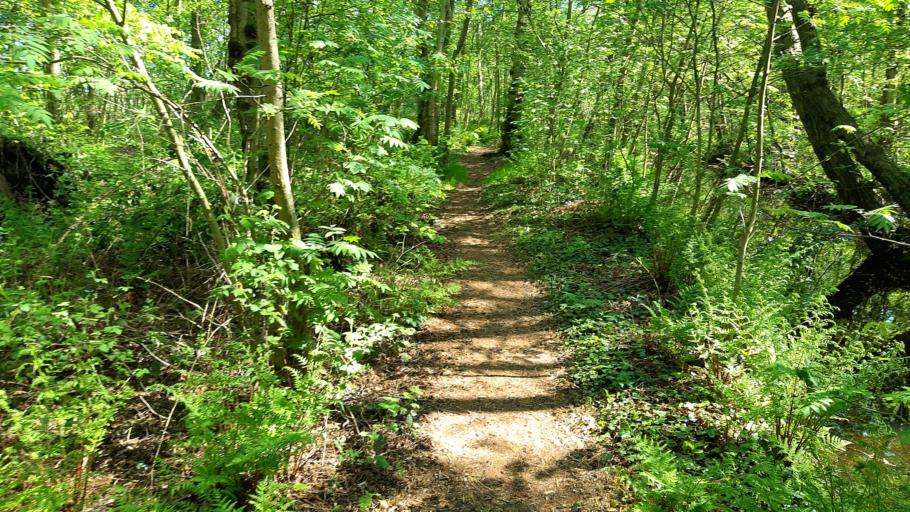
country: NL
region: South Holland
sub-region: Gemeente Gouda
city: Gouda
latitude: 51.9793
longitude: 4.6803
